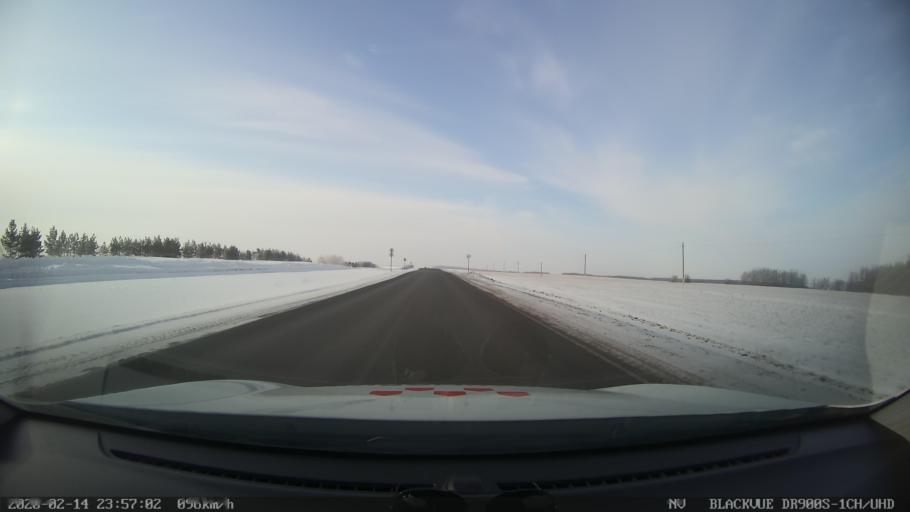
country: RU
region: Tatarstan
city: Kuybyshevskiy Zaton
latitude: 55.3311
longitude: 49.1186
